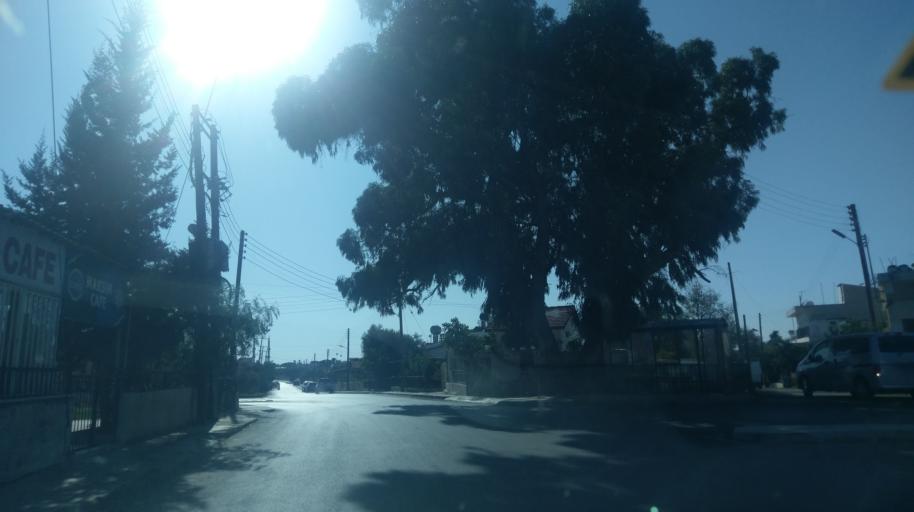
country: CY
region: Ammochostos
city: Famagusta
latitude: 35.1038
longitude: 33.9471
